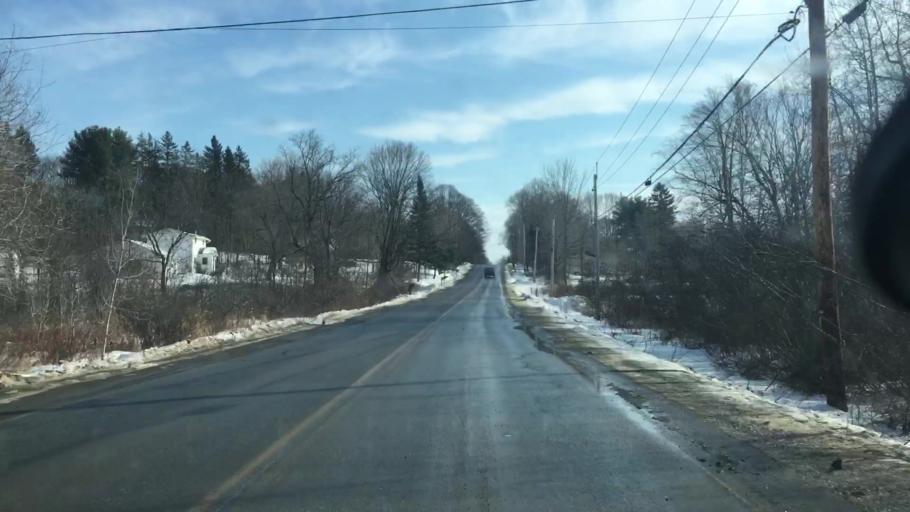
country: US
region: Maine
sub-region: Penobscot County
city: Bangor
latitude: 44.8504
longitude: -68.8420
